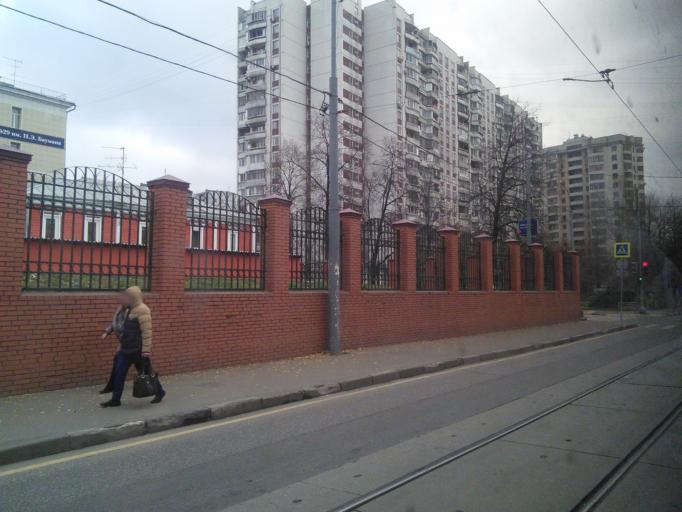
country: RU
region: Moscow
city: Lefortovo
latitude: 55.7656
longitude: 37.7008
